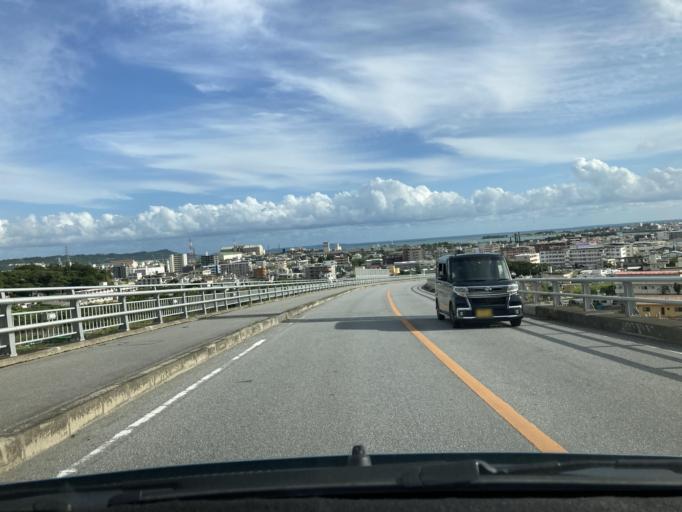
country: JP
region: Okinawa
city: Okinawa
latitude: 26.3395
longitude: 127.8335
